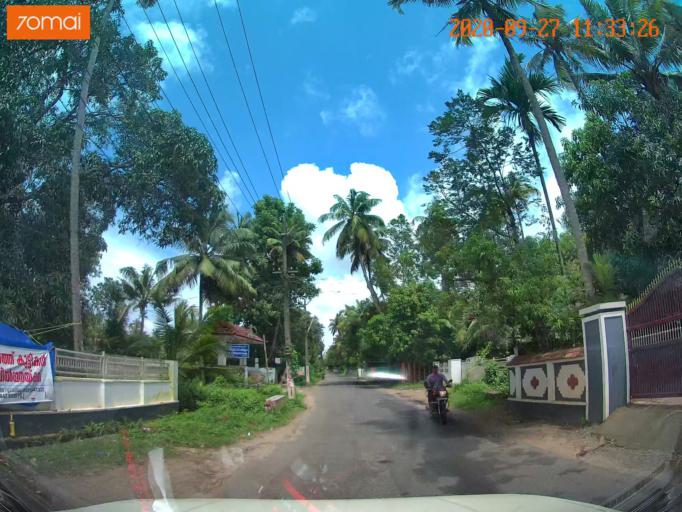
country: IN
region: Kerala
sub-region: Thrissur District
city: Thanniyam
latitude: 10.4308
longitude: 76.1292
